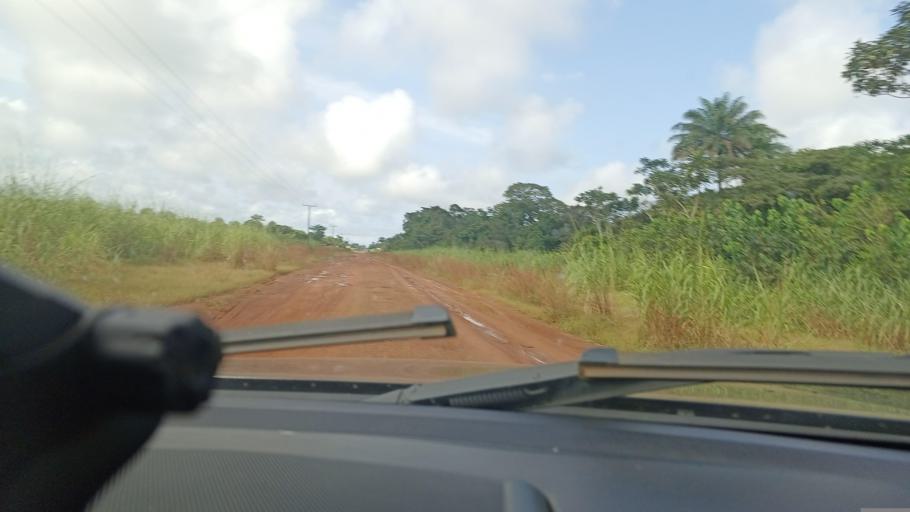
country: LR
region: Grand Cape Mount
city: Robertsport
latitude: 6.6966
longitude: -11.1014
